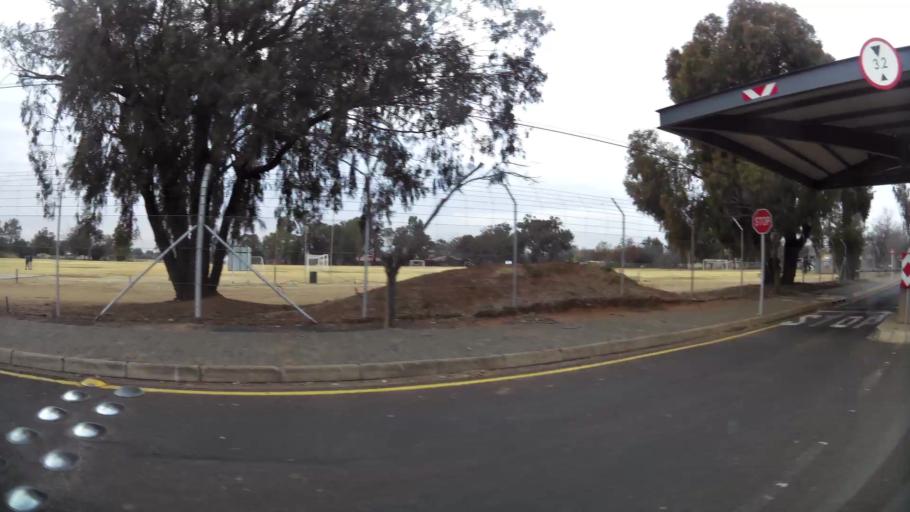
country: ZA
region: Orange Free State
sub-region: Mangaung Metropolitan Municipality
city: Bloemfontein
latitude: -29.1153
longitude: 26.1909
